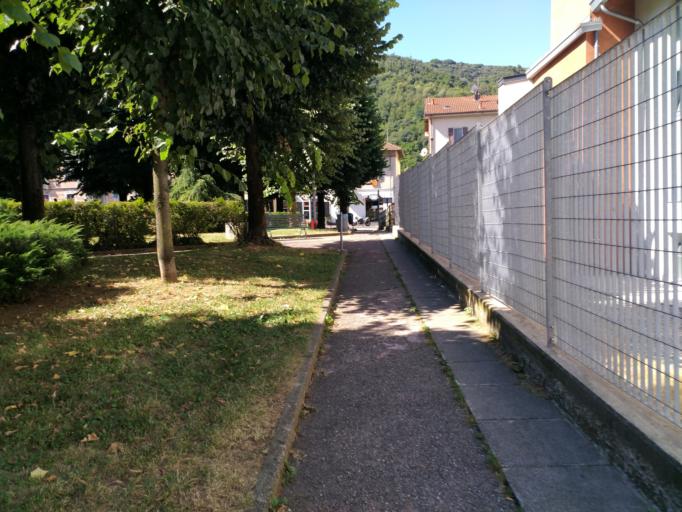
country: CH
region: Ticino
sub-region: Mendrisio District
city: Chiasso
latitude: 45.8313
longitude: 9.0378
